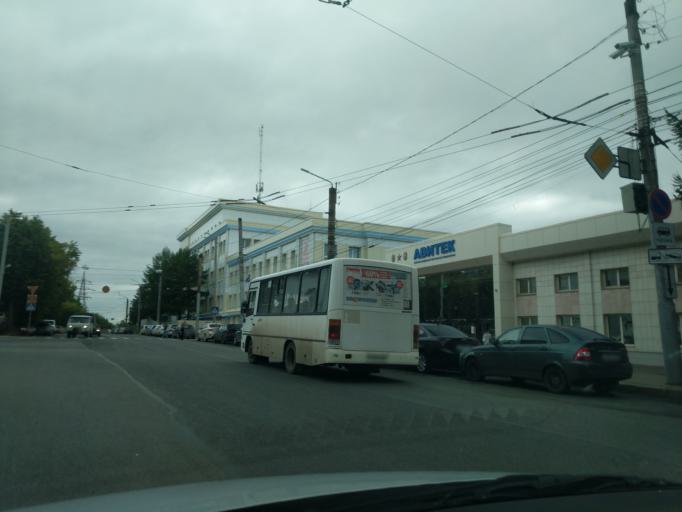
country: RU
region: Kirov
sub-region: Kirovo-Chepetskiy Rayon
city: Kirov
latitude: 58.6371
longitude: 49.6119
